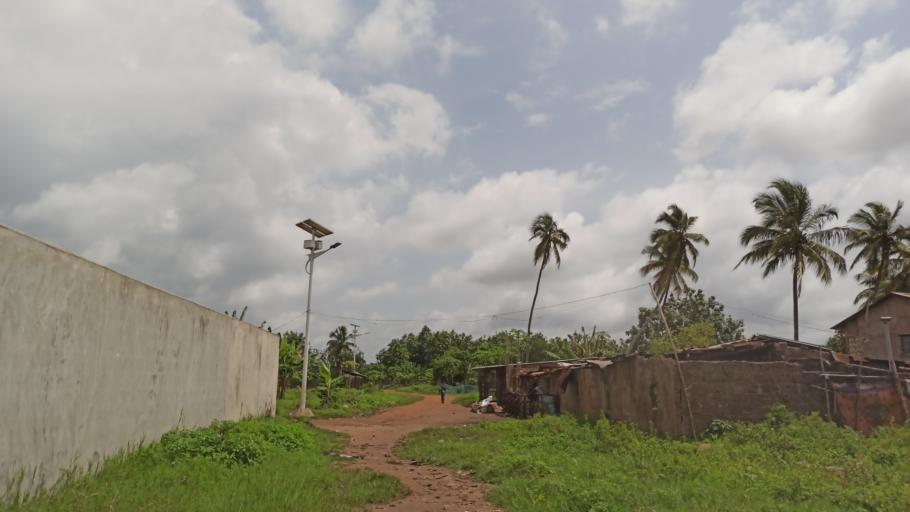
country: BJ
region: Queme
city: Porto-Novo
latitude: 6.4673
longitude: 2.6311
